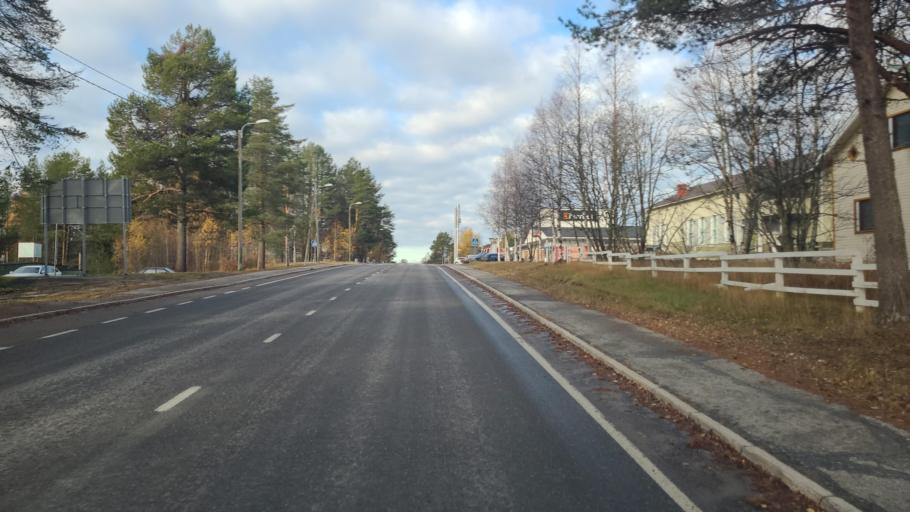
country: FI
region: Lapland
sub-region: Itae-Lappi
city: Posio
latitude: 66.1094
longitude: 28.1738
